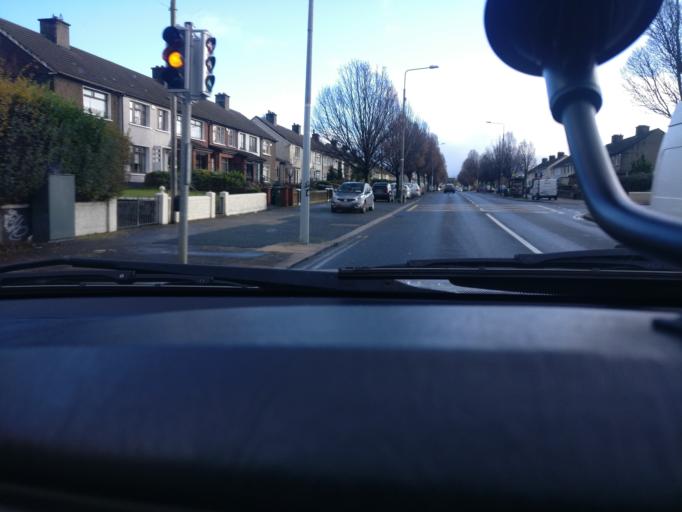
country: IE
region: Leinster
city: Crumlin
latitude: 53.3197
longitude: -6.3369
